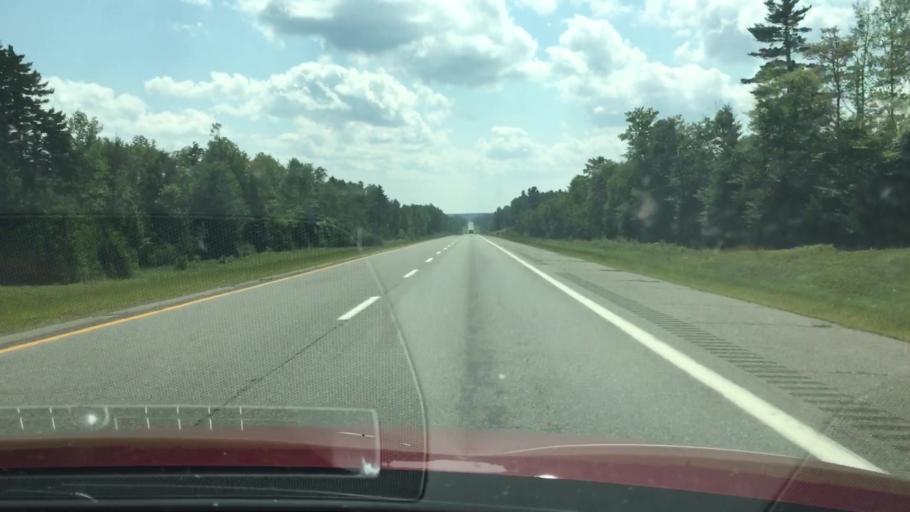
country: US
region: Maine
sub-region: Penobscot County
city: Lincoln
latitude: 45.4168
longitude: -68.5929
